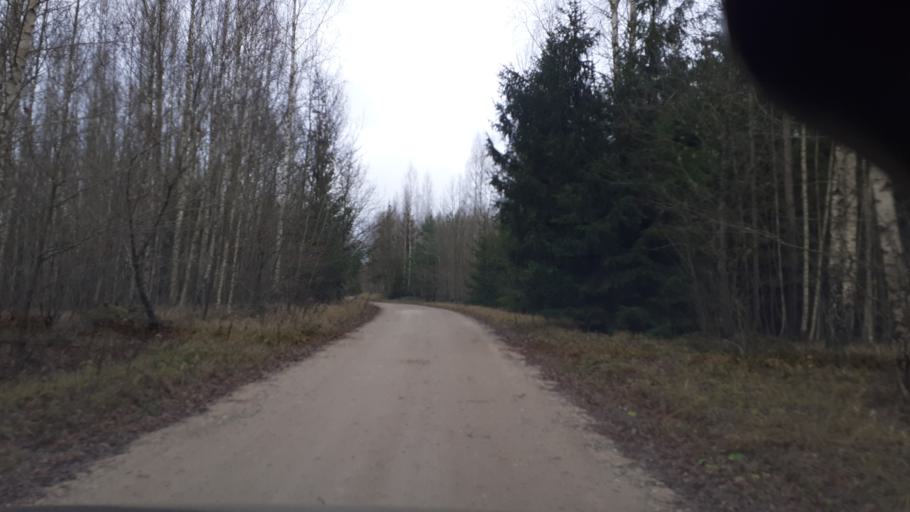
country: LV
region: Kuldigas Rajons
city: Kuldiga
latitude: 57.0294
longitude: 21.8704
